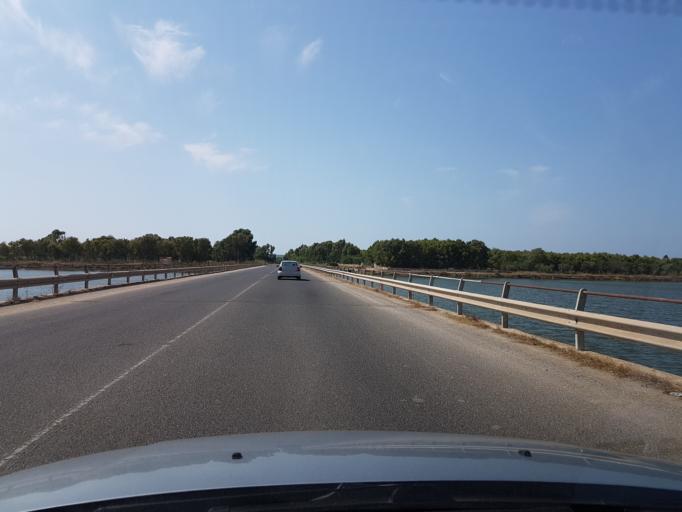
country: IT
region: Sardinia
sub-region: Provincia di Oristano
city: Cabras
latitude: 39.9168
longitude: 8.4989
